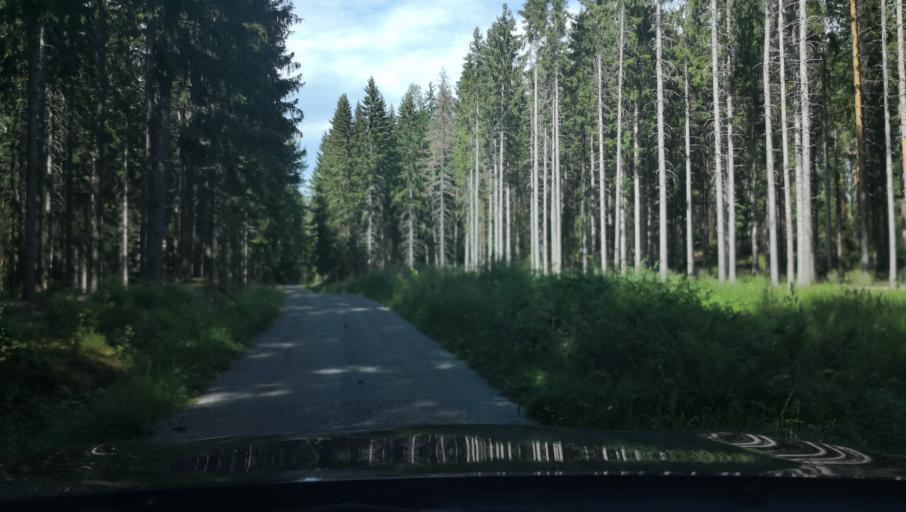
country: SE
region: Vaestmanland
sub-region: Surahammars Kommun
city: Ramnas
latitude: 59.9468
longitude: 16.1940
